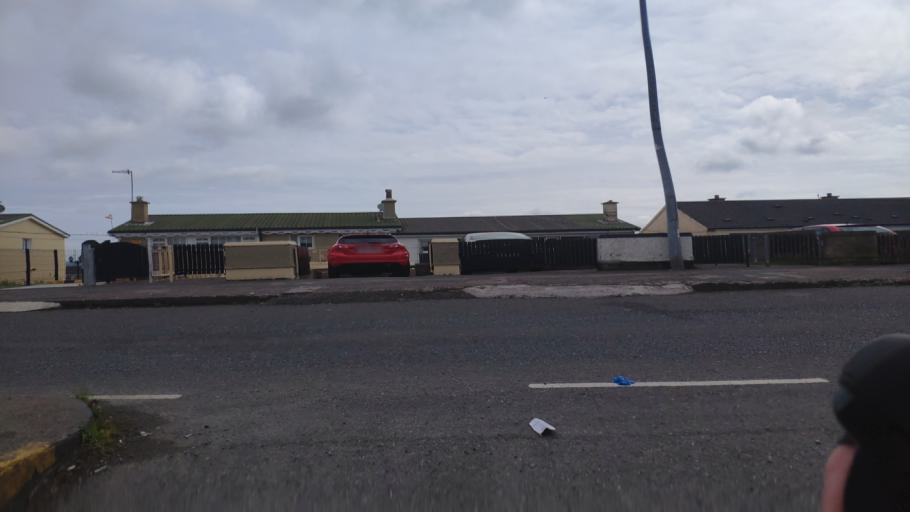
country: IE
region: Munster
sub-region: County Cork
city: Cork
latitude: 51.9079
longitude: -8.5054
